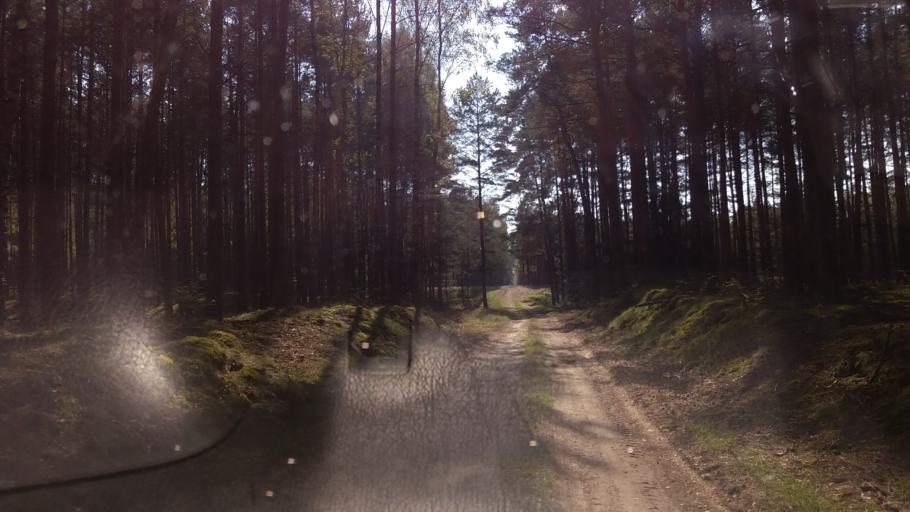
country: PL
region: West Pomeranian Voivodeship
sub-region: Powiat drawski
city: Kalisz Pomorski
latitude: 53.1980
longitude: 15.8951
